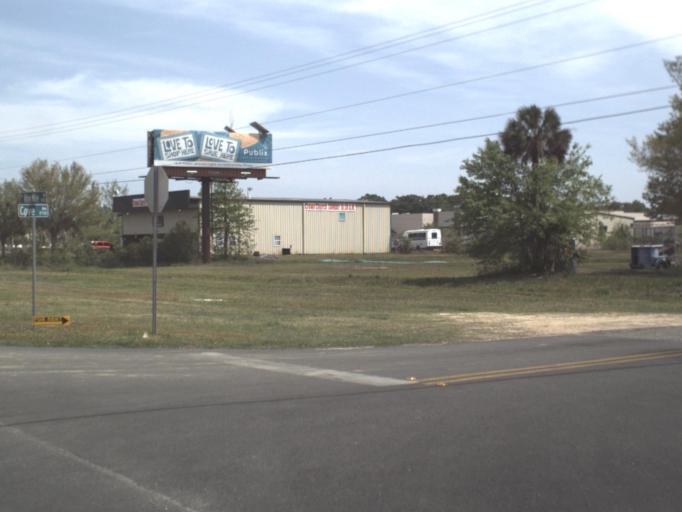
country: US
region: Florida
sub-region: Escambia County
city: Ensley
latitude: 30.5336
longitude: -87.2881
